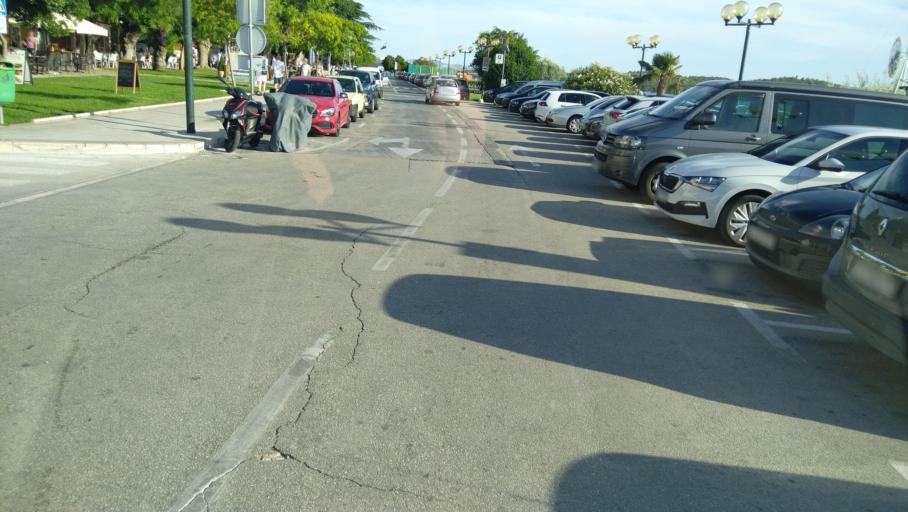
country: HR
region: Sibensko-Kniniska
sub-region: Grad Sibenik
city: Sibenik
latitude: 43.7363
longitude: 15.8881
